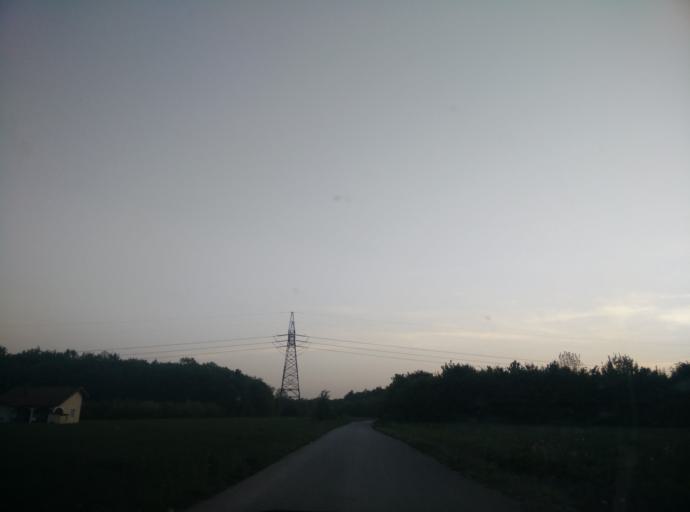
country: BA
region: Brcko
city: Brcko
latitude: 44.7752
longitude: 18.8407
